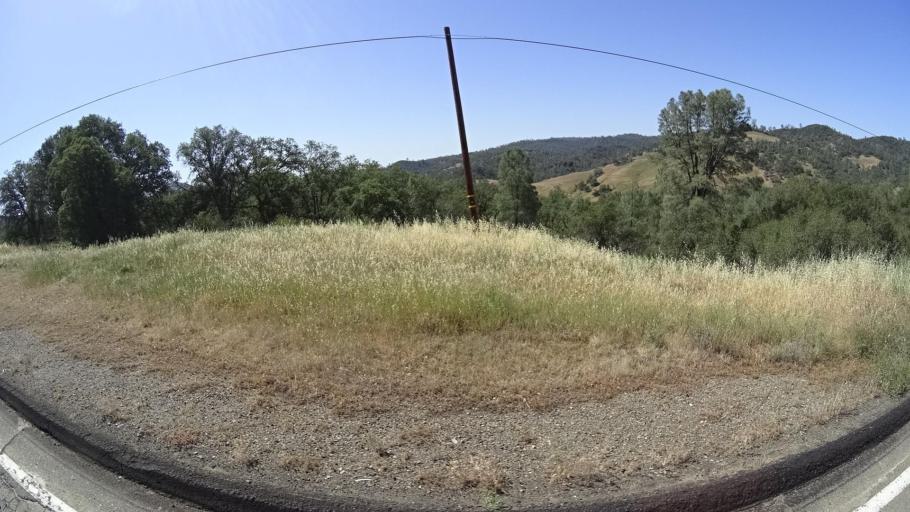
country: US
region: California
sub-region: Lake County
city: Hidden Valley Lake
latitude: 38.8783
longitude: -122.5272
